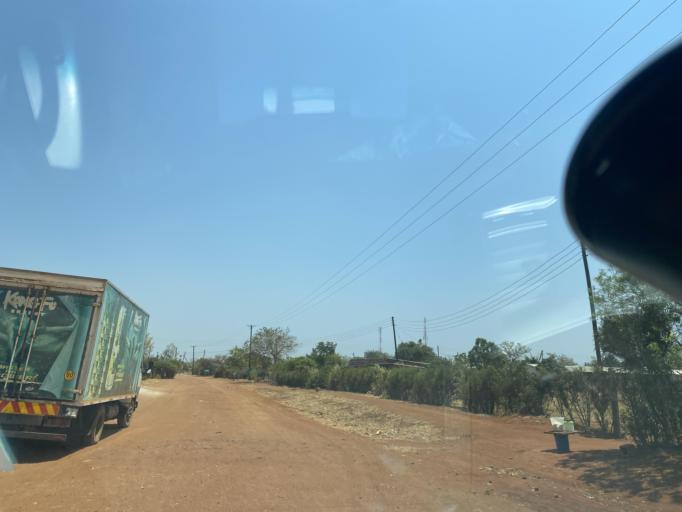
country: ZM
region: Southern
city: Nakambala
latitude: -15.5135
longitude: 27.9310
